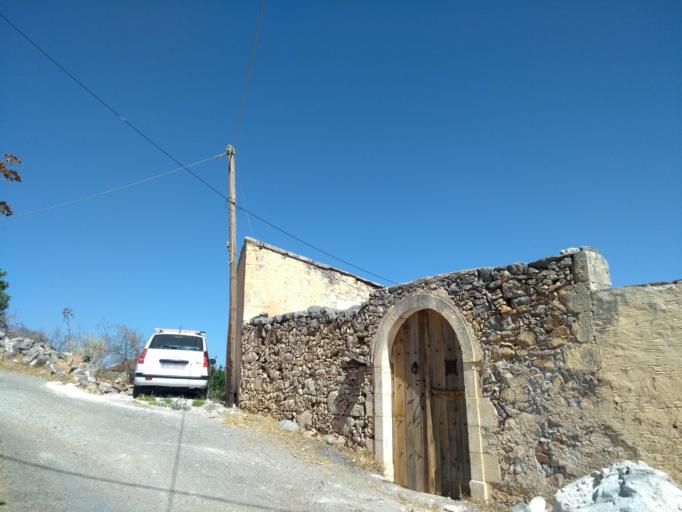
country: GR
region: Crete
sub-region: Nomos Chanias
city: Georgioupolis
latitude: 35.3958
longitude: 24.2341
